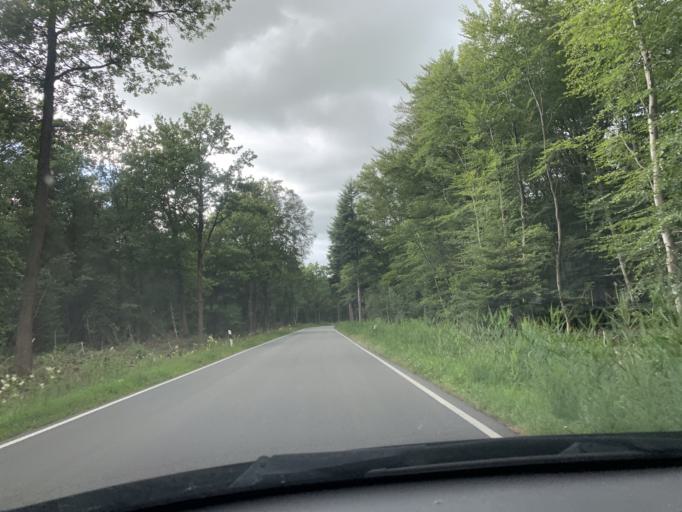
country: DE
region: Lower Saxony
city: Westerstede
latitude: 53.2167
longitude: 7.9177
